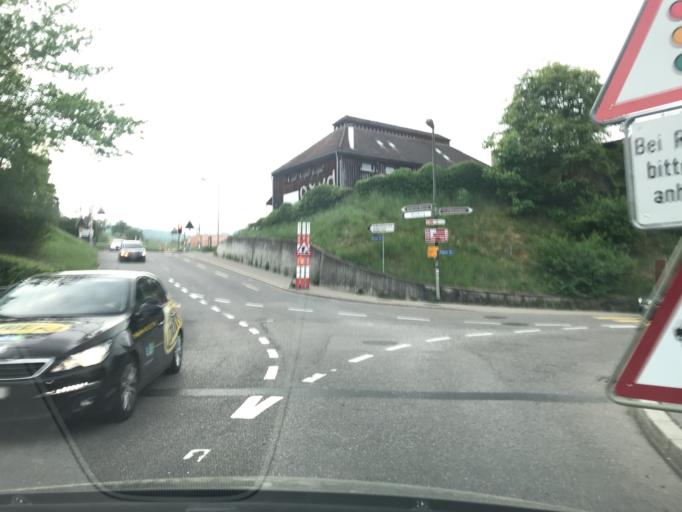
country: CH
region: Zurich
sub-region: Bezirk Winterthur
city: Wuelflingen (Kreis 6)
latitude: 47.5057
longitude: 8.6834
